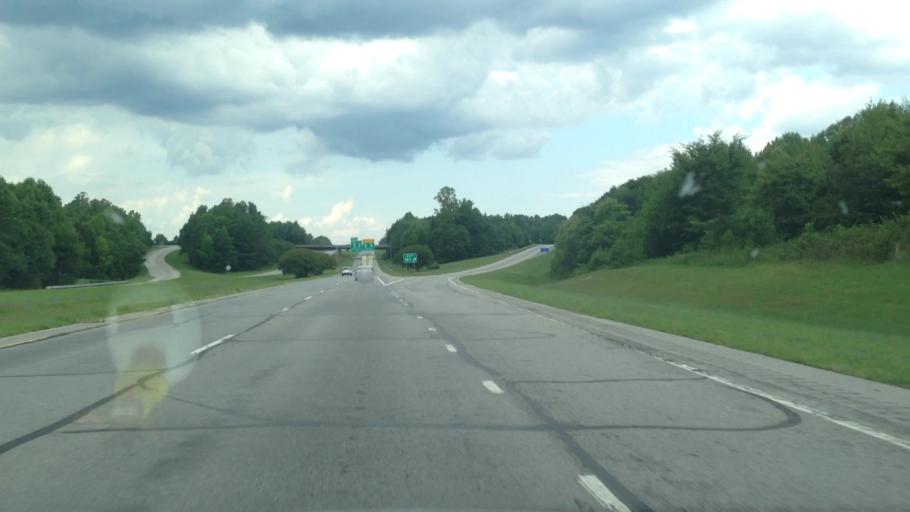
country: US
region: Virginia
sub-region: City of Danville
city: Danville
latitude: 36.5144
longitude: -79.4759
